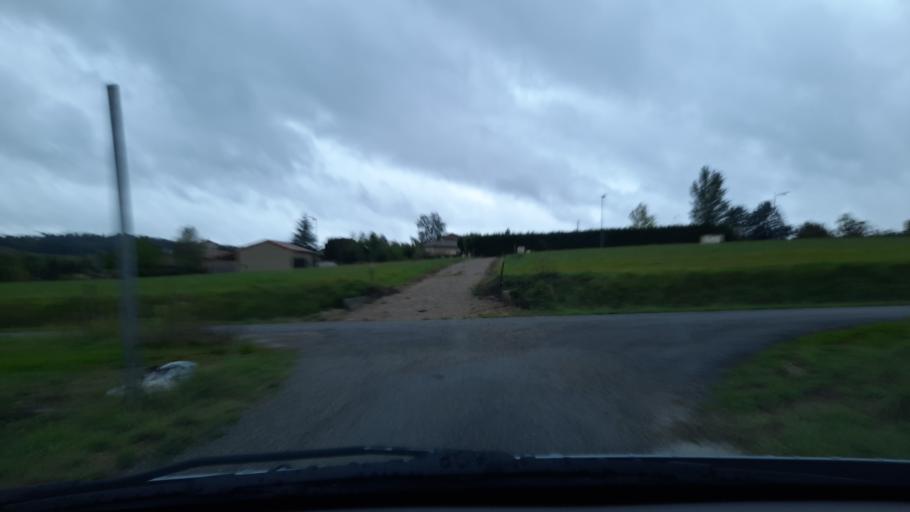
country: FR
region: Midi-Pyrenees
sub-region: Departement du Tarn-et-Garonne
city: Molieres
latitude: 44.1936
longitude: 1.2859
